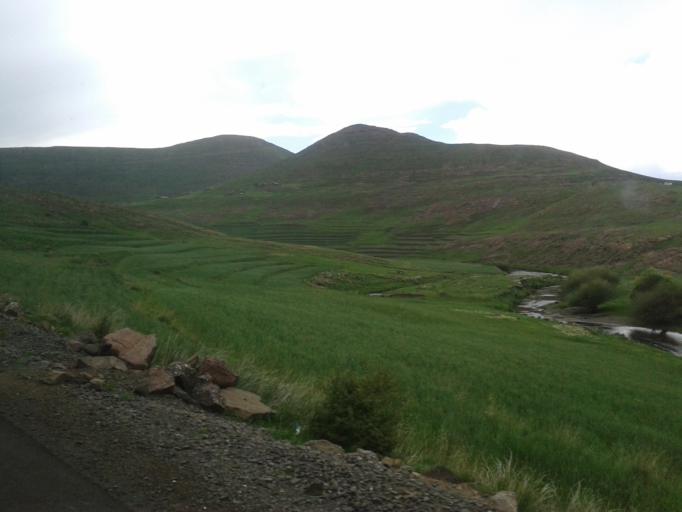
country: LS
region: Maseru
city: Nako
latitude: -29.8045
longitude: 28.0293
